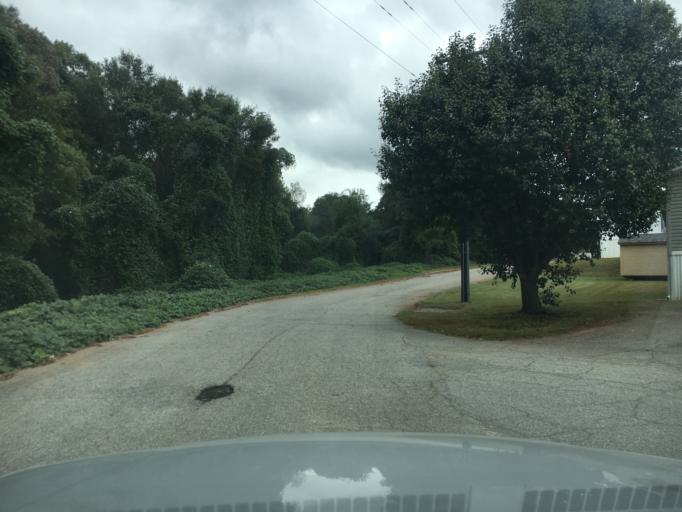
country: US
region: South Carolina
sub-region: Spartanburg County
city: Duncan
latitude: 34.9262
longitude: -82.1383
